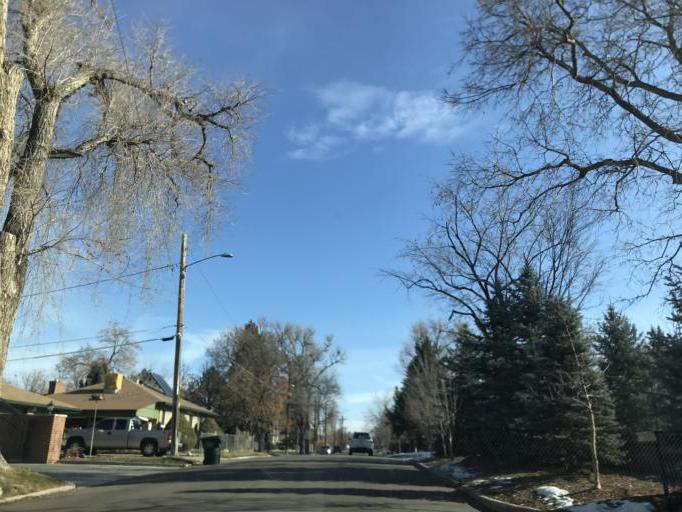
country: US
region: Colorado
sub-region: Arapahoe County
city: Glendale
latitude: 39.7356
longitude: -104.9067
